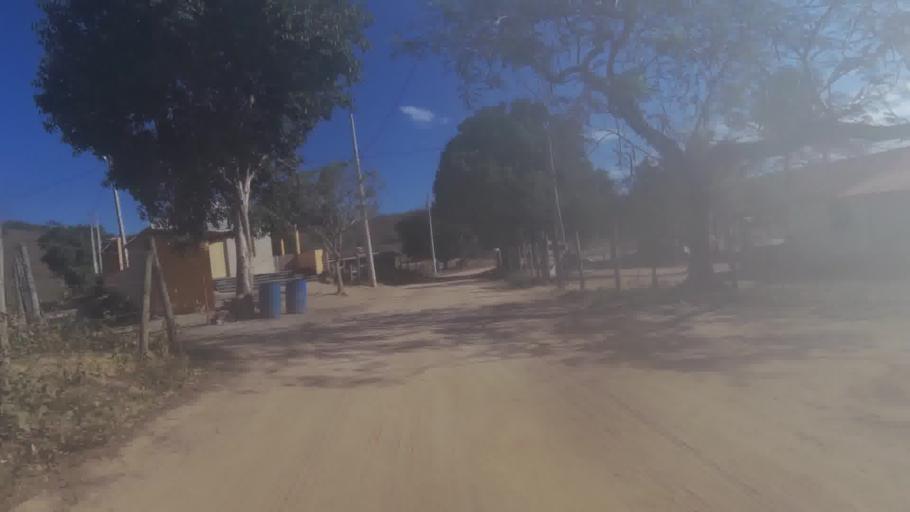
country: BR
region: Espirito Santo
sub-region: Cachoeiro De Itapemirim
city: Cachoeiro de Itapemirim
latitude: -21.0181
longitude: -41.0390
